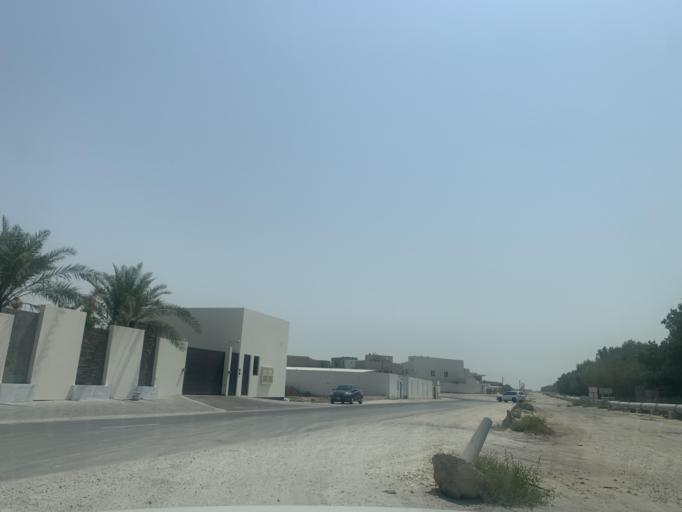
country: BH
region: Central Governorate
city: Madinat Hamad
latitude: 26.1439
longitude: 50.4724
